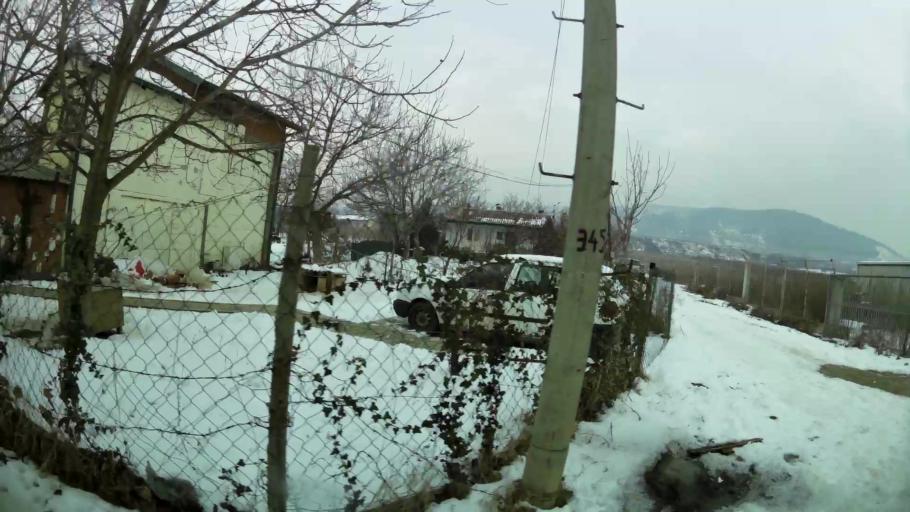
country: MK
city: Kondovo
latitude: 42.0389
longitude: 21.3396
